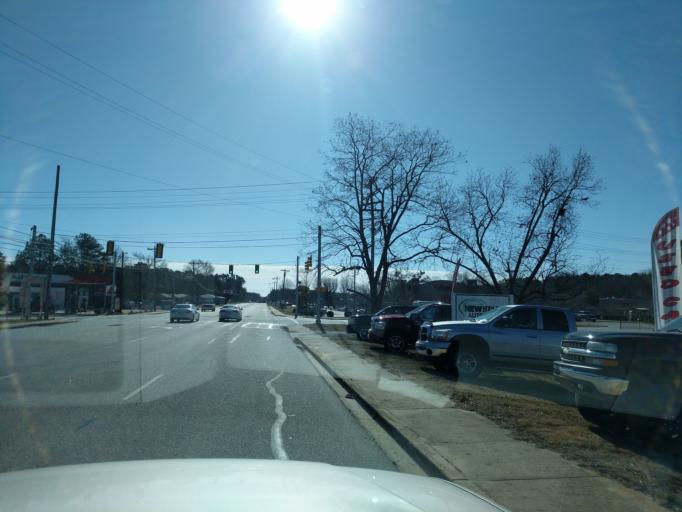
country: US
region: South Carolina
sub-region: Laurens County
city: Clinton
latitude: 34.4546
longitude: -81.8765
